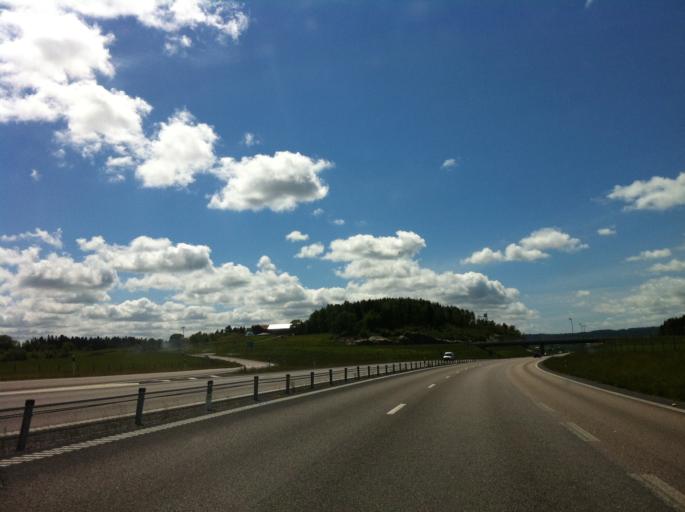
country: SE
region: Vaestra Goetaland
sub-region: Trollhattan
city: Sjuntorp
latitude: 58.2111
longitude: 12.1821
